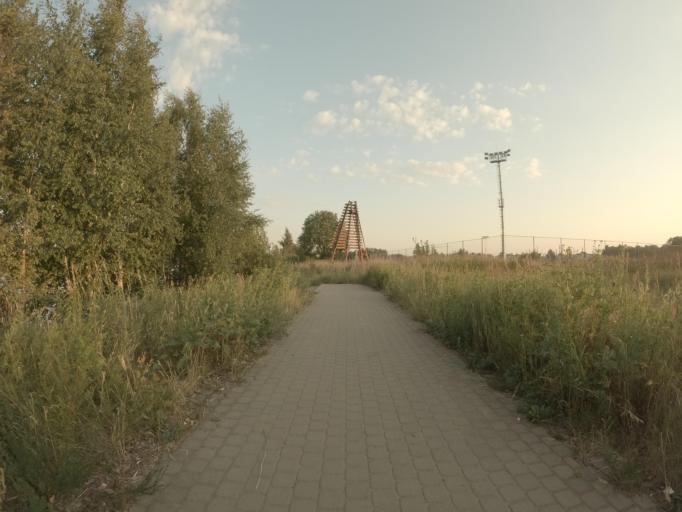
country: RU
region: Leningrad
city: Kirovsk
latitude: 59.8493
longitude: 30.9451
